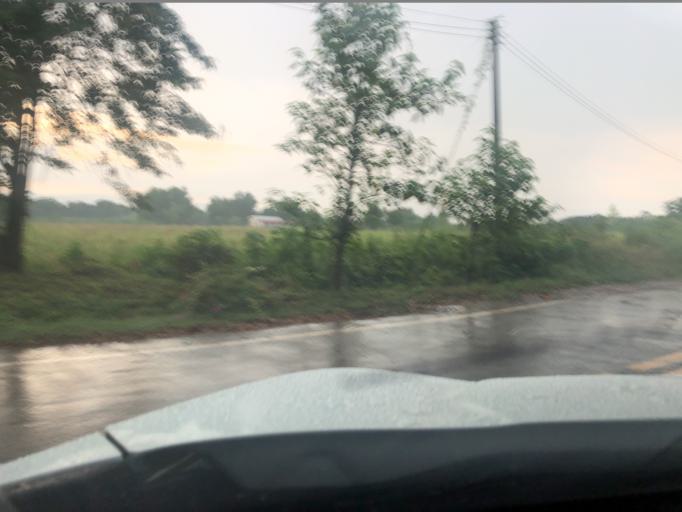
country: TH
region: Lop Buri
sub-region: Amphoe Tha Luang
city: Tha Luang
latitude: 15.0462
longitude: 101.2376
